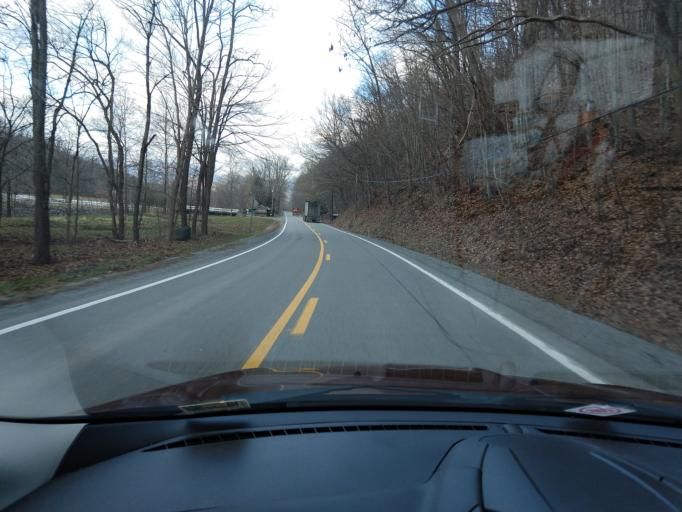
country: US
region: West Virginia
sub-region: Randolph County
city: Elkins
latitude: 38.6749
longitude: -79.9529
